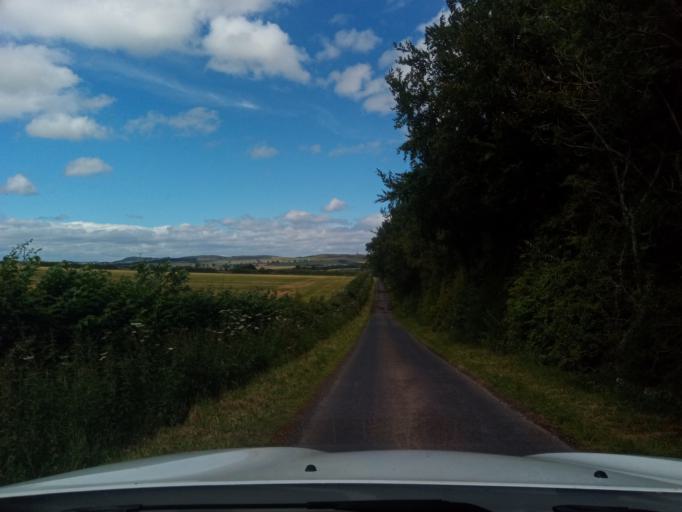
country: GB
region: Scotland
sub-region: The Scottish Borders
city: Jedburgh
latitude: 55.5657
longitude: -2.5456
